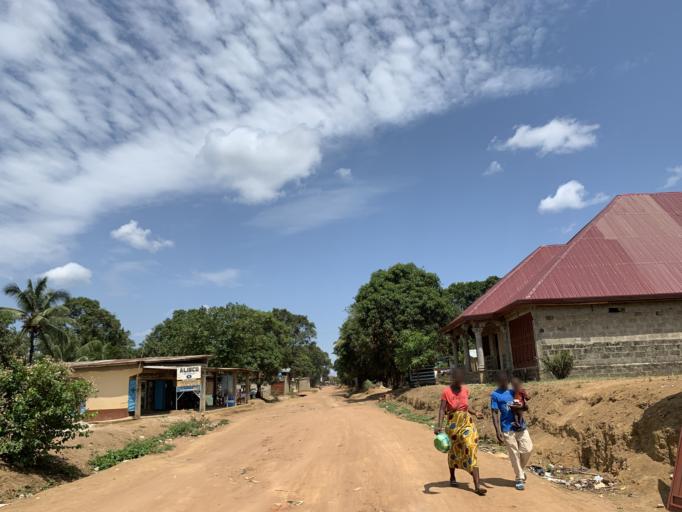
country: SL
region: Western Area
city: Waterloo
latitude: 8.3324
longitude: -13.0414
